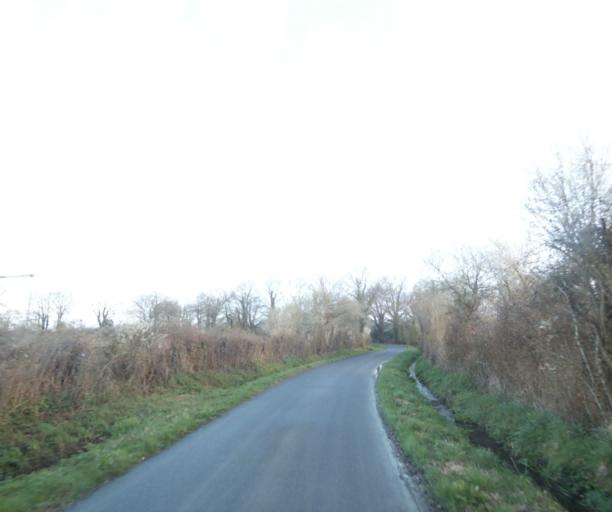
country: FR
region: Pays de la Loire
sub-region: Departement de la Loire-Atlantique
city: Savenay
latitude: 47.3935
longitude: -1.9138
